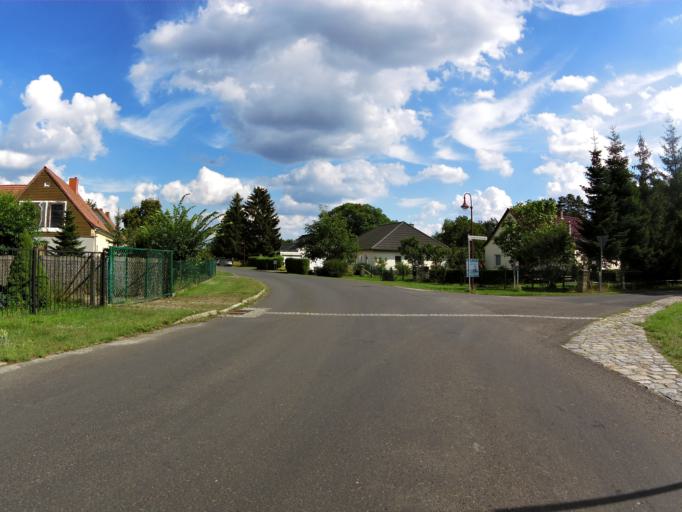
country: DE
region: Brandenburg
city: Munchehofe
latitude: 52.1928
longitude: 13.8735
